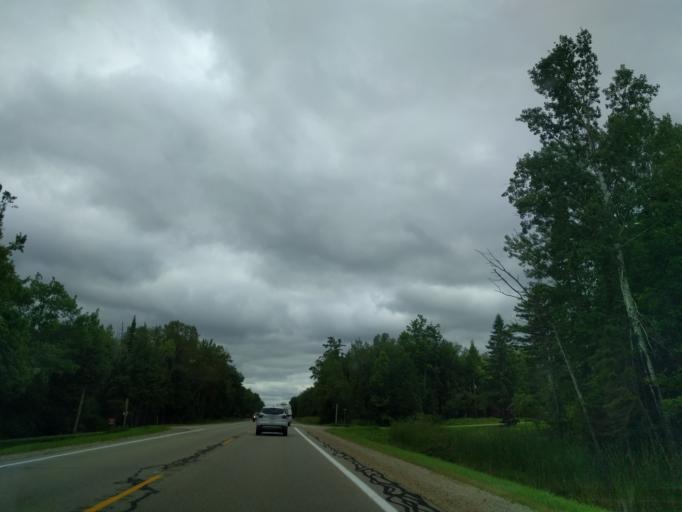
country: US
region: Michigan
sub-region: Menominee County
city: Menominee
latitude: 45.3462
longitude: -87.4099
